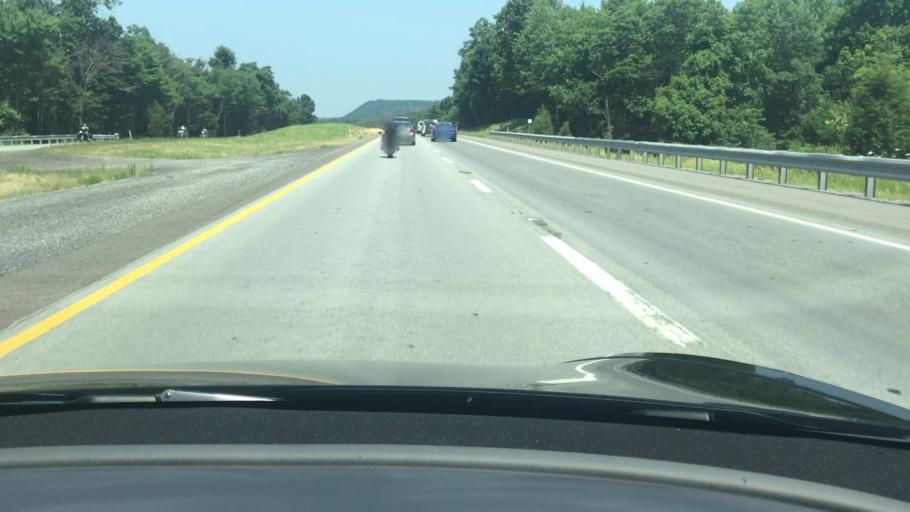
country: US
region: Pennsylvania
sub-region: Perry County
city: Duncannon
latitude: 40.4387
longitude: -77.0140
